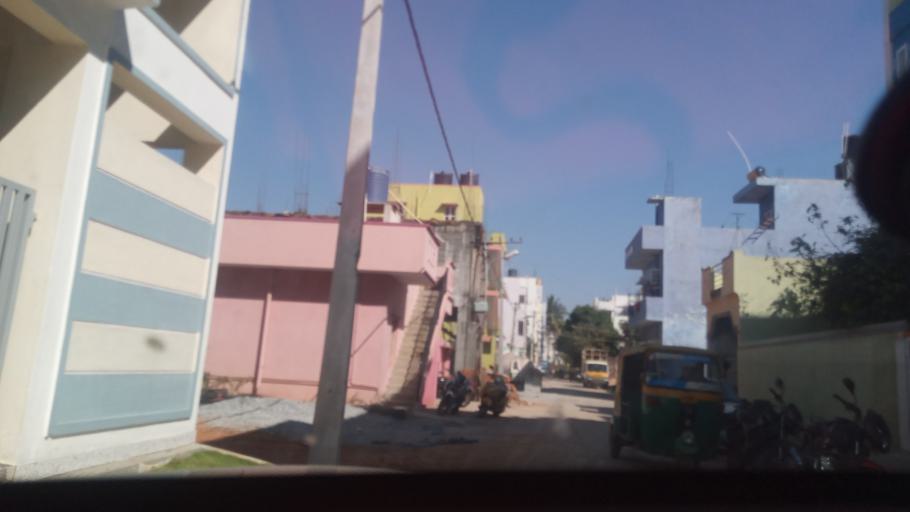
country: IN
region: Karnataka
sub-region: Bangalore Urban
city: Yelahanka
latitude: 13.0414
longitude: 77.4981
